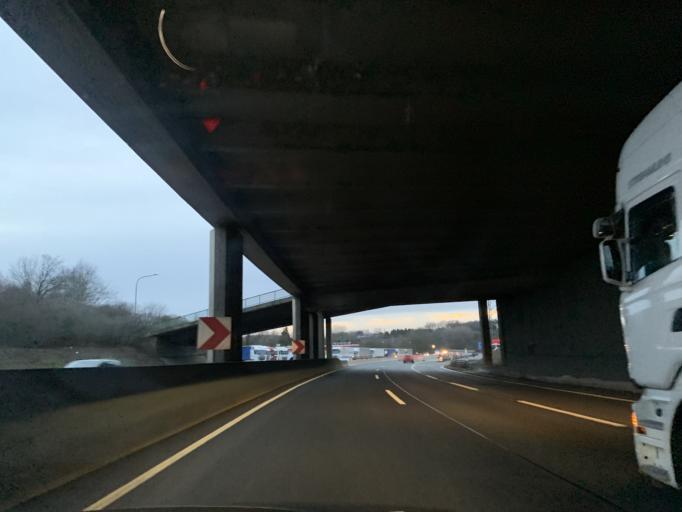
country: DE
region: North Rhine-Westphalia
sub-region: Regierungsbezirk Dusseldorf
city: Wuppertal
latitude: 51.2972
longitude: 7.2166
